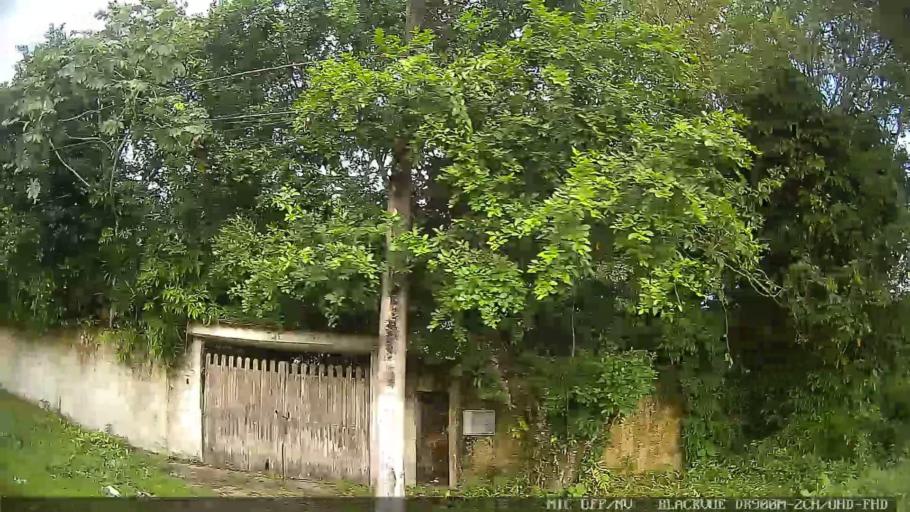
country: BR
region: Sao Paulo
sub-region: Itanhaem
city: Itanhaem
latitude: -24.2164
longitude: -46.8784
